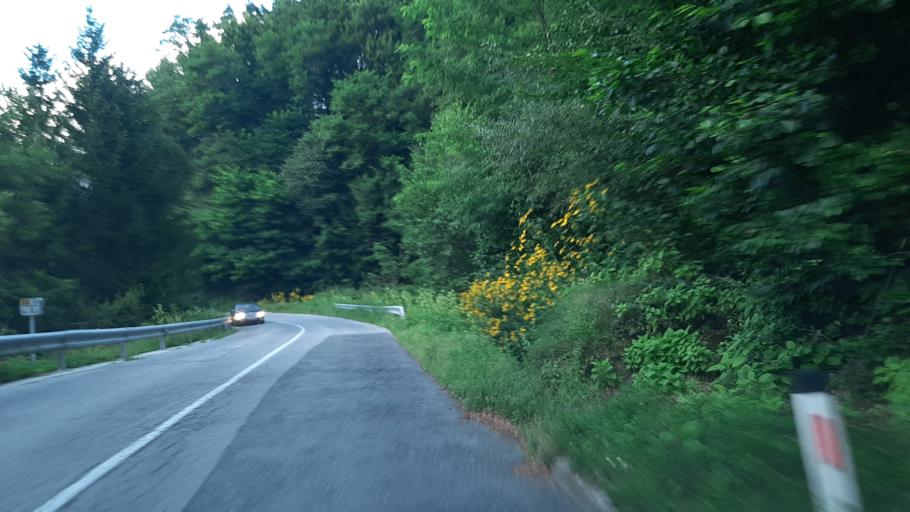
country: SI
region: Dobje
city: Dobje pri Planini
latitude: 46.1530
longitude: 15.4409
